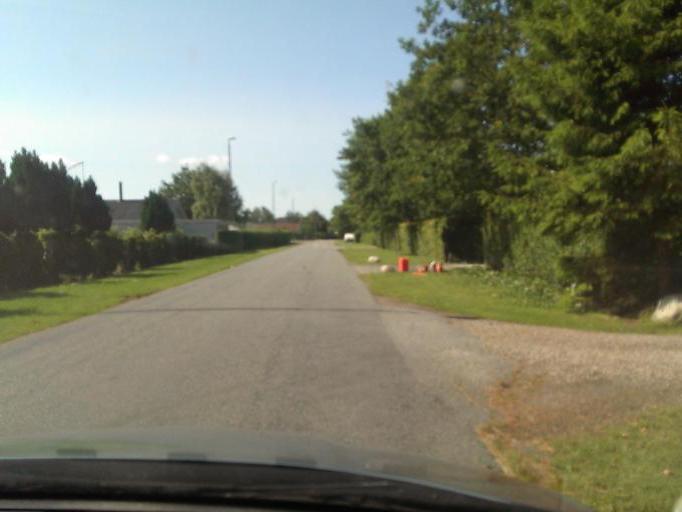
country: DK
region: North Denmark
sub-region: Jammerbugt Kommune
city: Abybro
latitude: 57.1698
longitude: 9.7357
